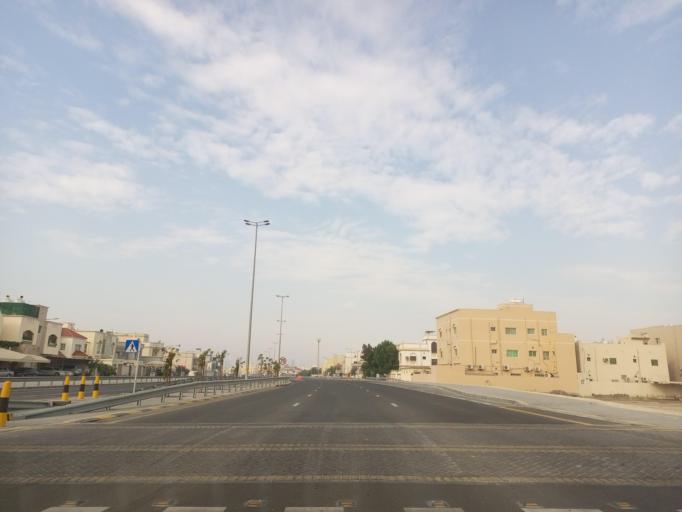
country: BH
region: Muharraq
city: Al Hadd
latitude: 26.2475
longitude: 50.6459
